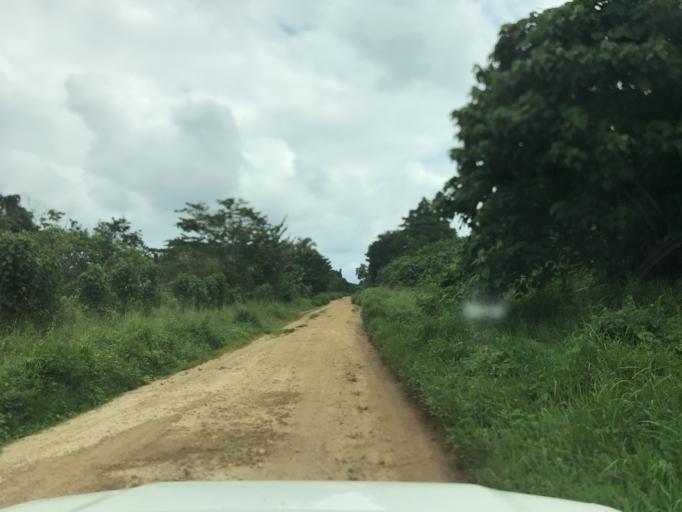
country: VU
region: Sanma
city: Port-Olry
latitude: -15.1868
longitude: 167.0088
